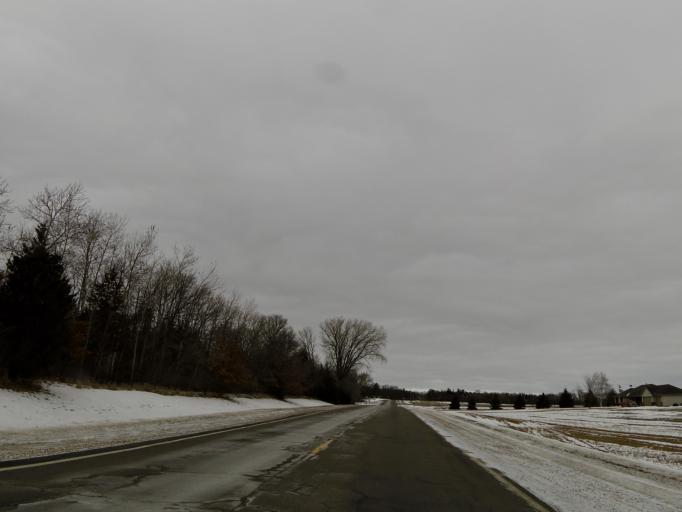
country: US
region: Minnesota
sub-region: Washington County
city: Cottage Grove
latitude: 44.8024
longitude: -92.8933
